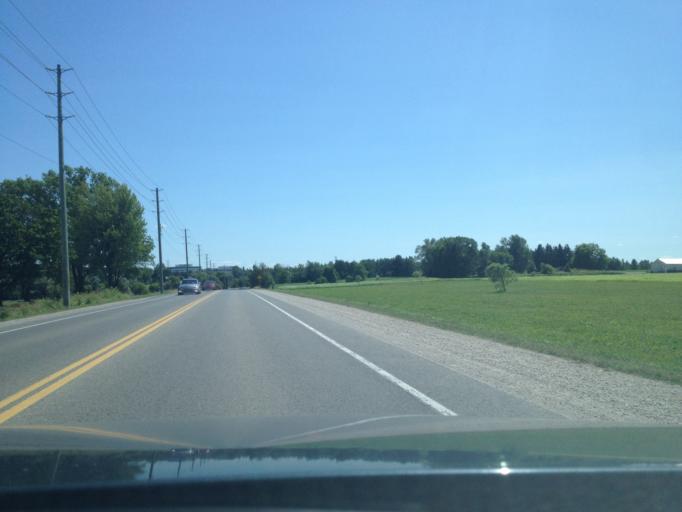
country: CA
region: Ontario
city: Waterloo
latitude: 43.5298
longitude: -80.5137
